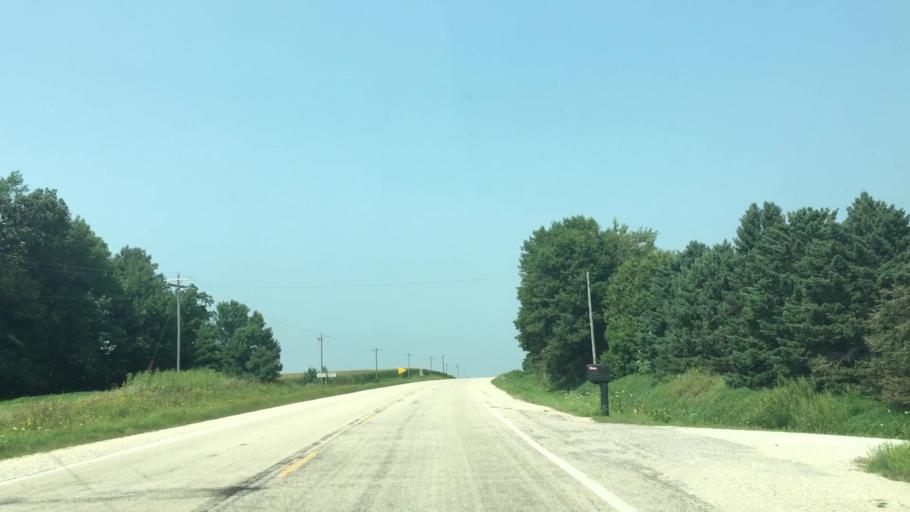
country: US
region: Iowa
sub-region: Fayette County
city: West Union
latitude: 43.0041
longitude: -91.8245
